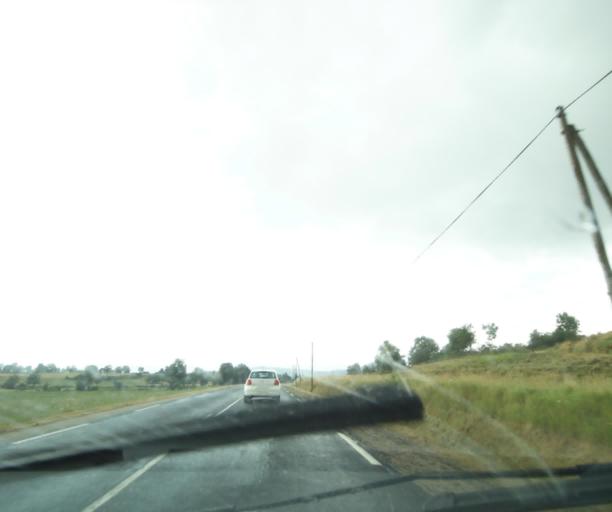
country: FR
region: Auvergne
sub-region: Departement de la Haute-Loire
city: Espaly-Saint-Marcel
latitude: 45.0274
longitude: 3.8445
